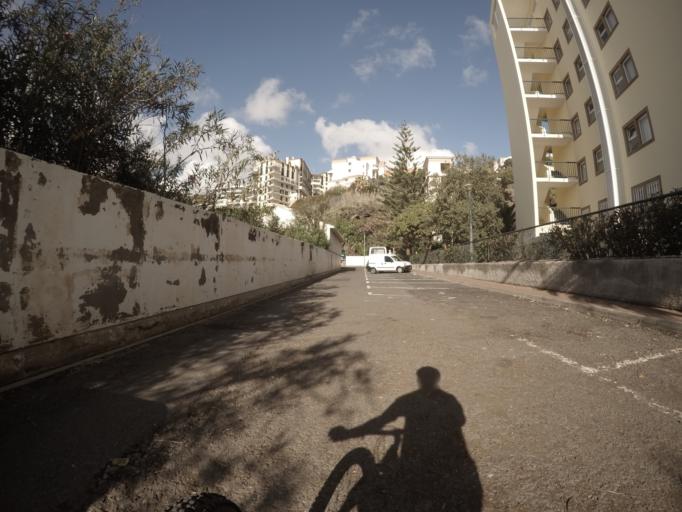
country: PT
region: Madeira
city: Camara de Lobos
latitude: 32.6392
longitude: -16.9506
